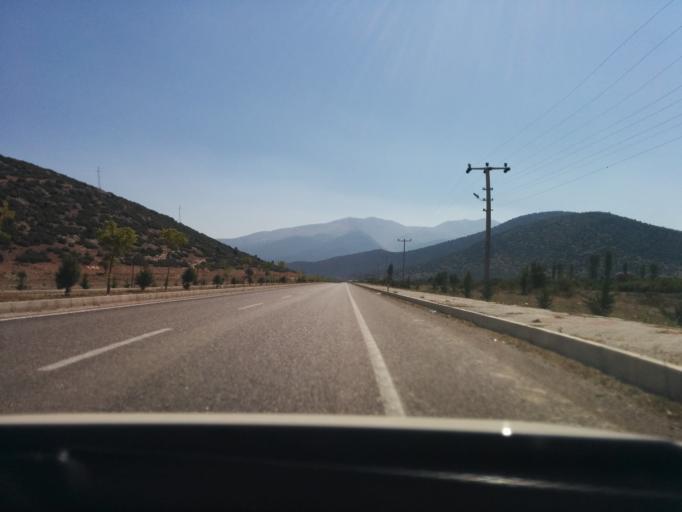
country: TR
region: Antalya
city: Korkuteli
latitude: 37.0330
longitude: 30.2558
